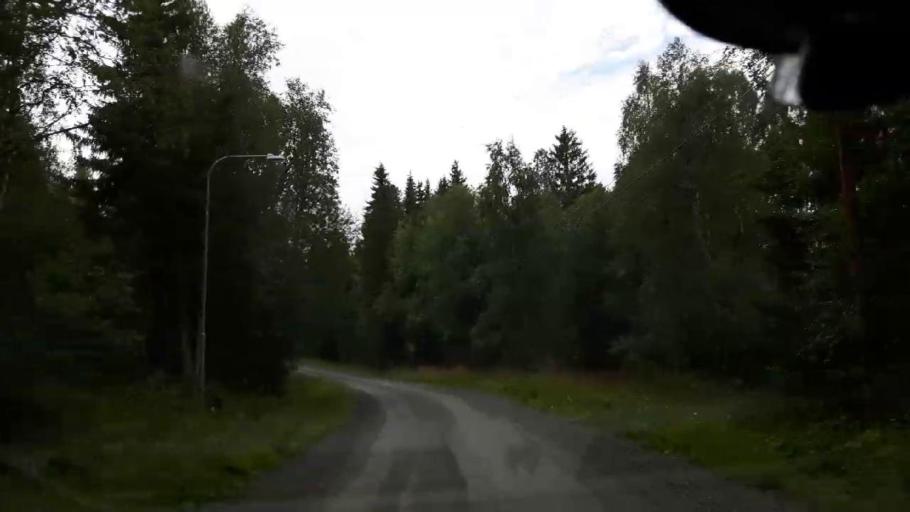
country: SE
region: Jaemtland
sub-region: Krokoms Kommun
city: Valla
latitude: 63.7021
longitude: 13.8735
